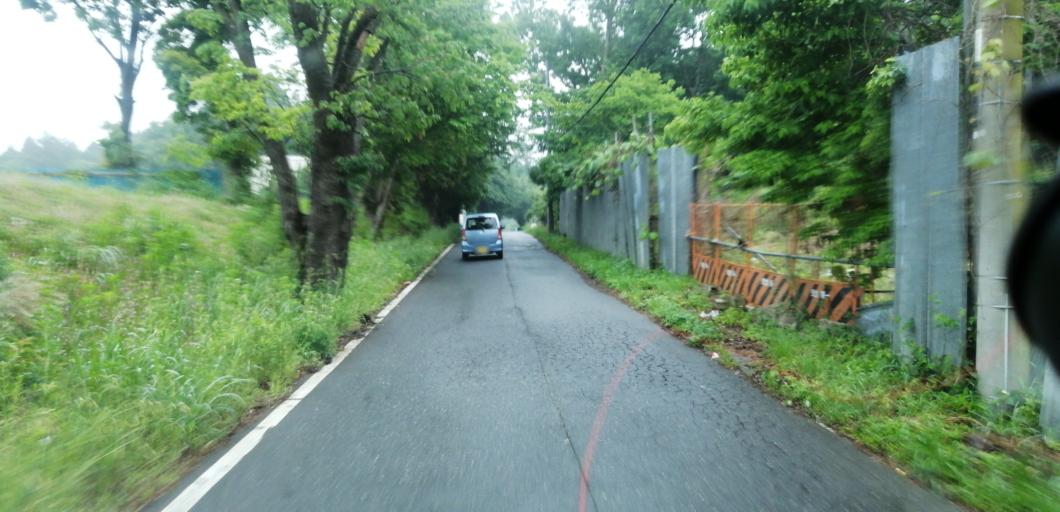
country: JP
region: Chiba
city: Ichihara
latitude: 35.4779
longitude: 140.1509
